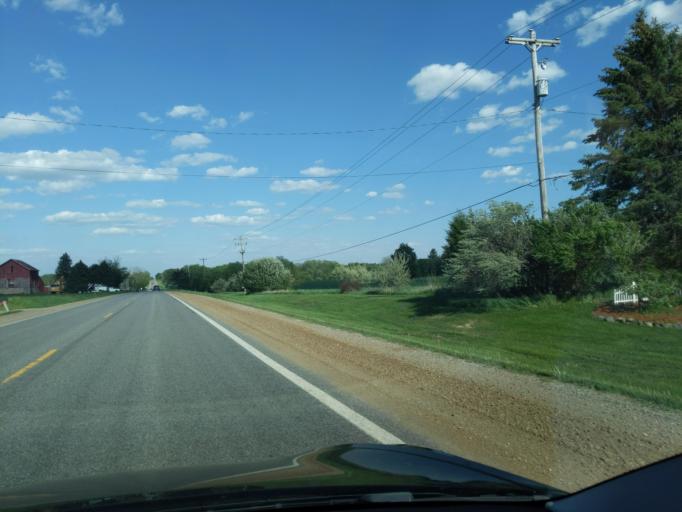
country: US
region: Michigan
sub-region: Ionia County
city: Portland
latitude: 42.7556
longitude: -84.9661
